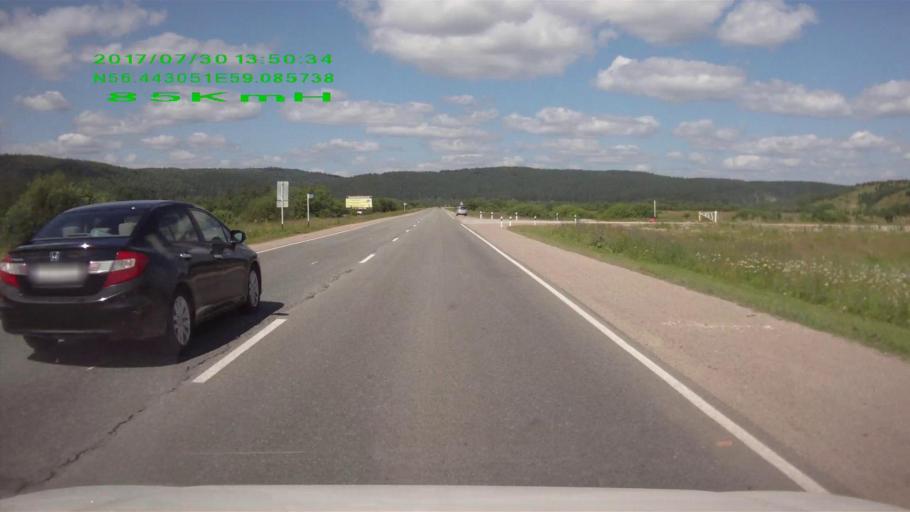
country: RU
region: Sverdlovsk
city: Mikhaylovsk
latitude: 56.4435
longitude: 59.0855
